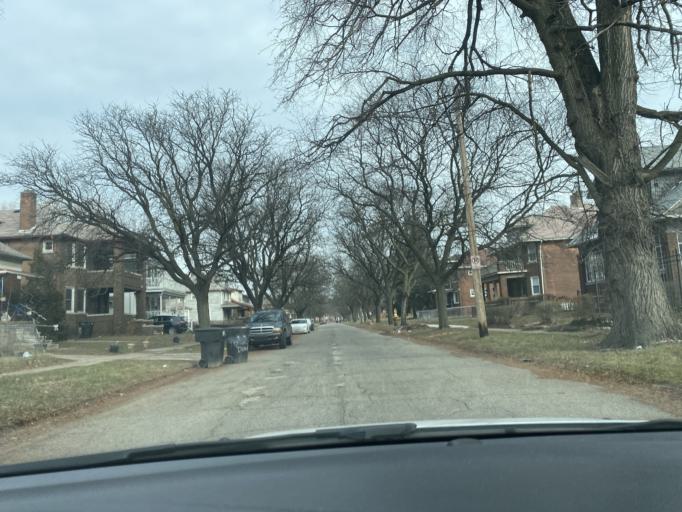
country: US
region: Michigan
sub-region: Wayne County
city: Highland Park
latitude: 42.3679
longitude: -83.1345
